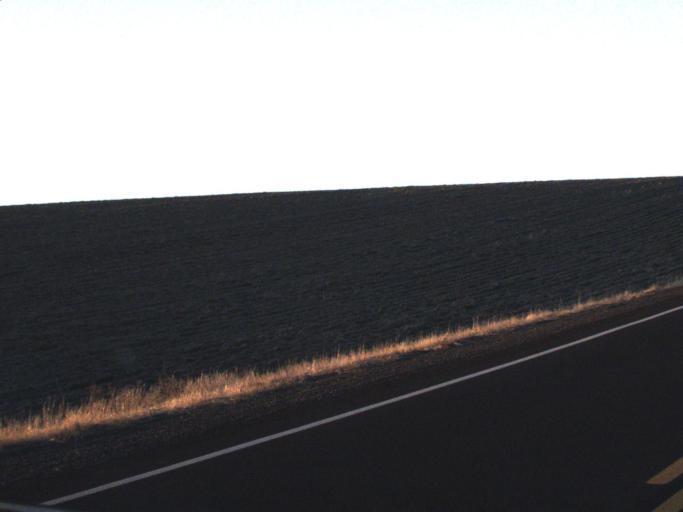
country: US
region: Washington
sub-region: Adams County
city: Ritzville
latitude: 47.0062
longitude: -118.6637
